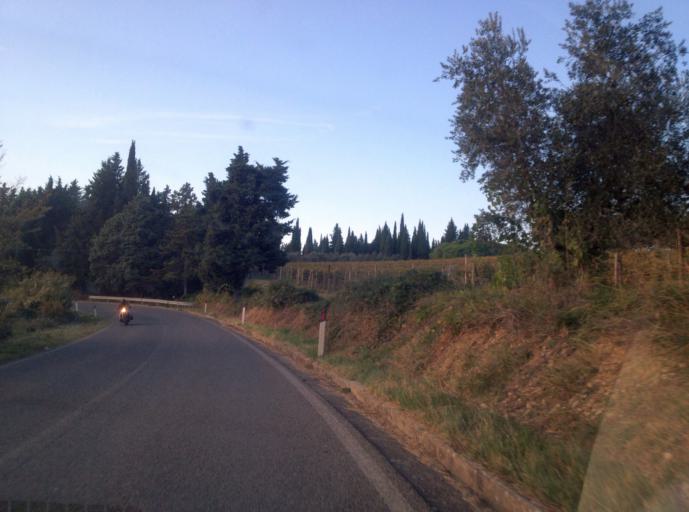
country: IT
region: Tuscany
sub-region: Provincia di Siena
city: Castellina in Chianti
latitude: 43.4474
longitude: 11.2978
